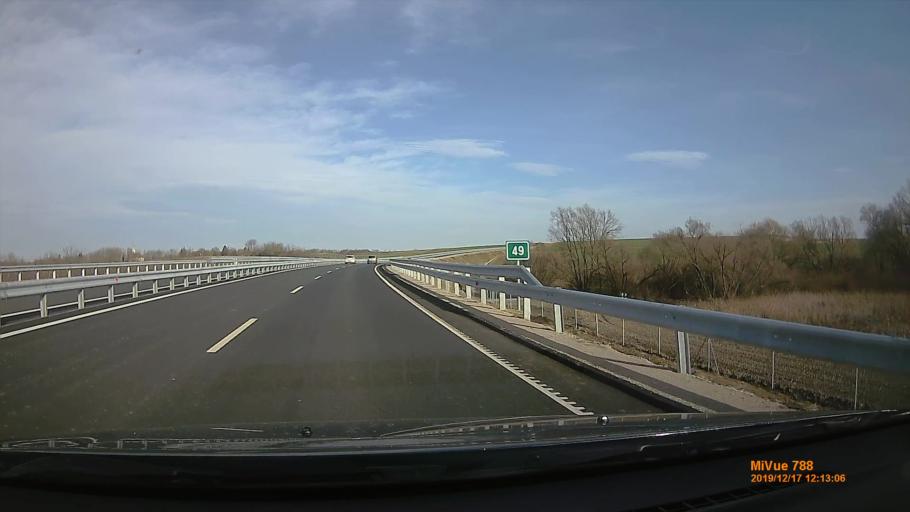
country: HU
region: Somogy
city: Kaposvar
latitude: 46.4513
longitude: 17.7713
